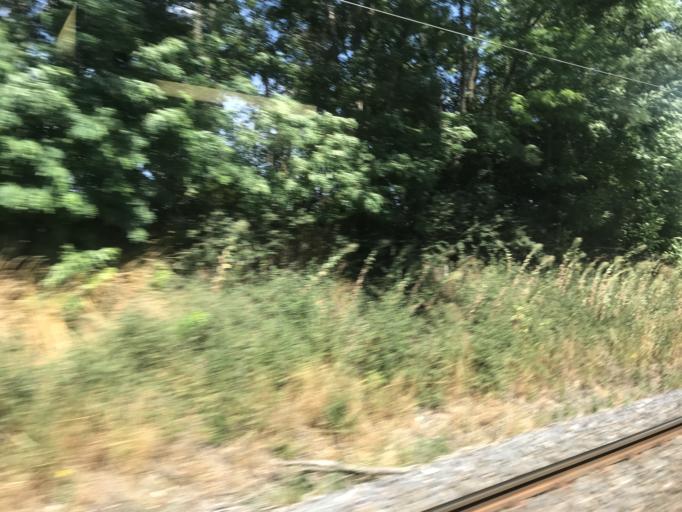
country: FR
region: Lorraine
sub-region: Departement de la Moselle
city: Crehange
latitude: 48.9647
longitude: 6.5650
